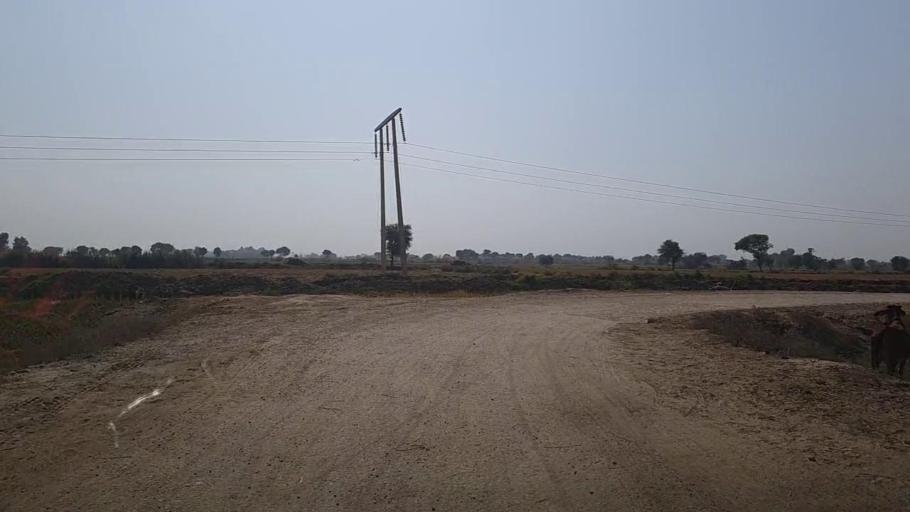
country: PK
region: Sindh
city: Kandhkot
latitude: 28.3885
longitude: 69.2929
